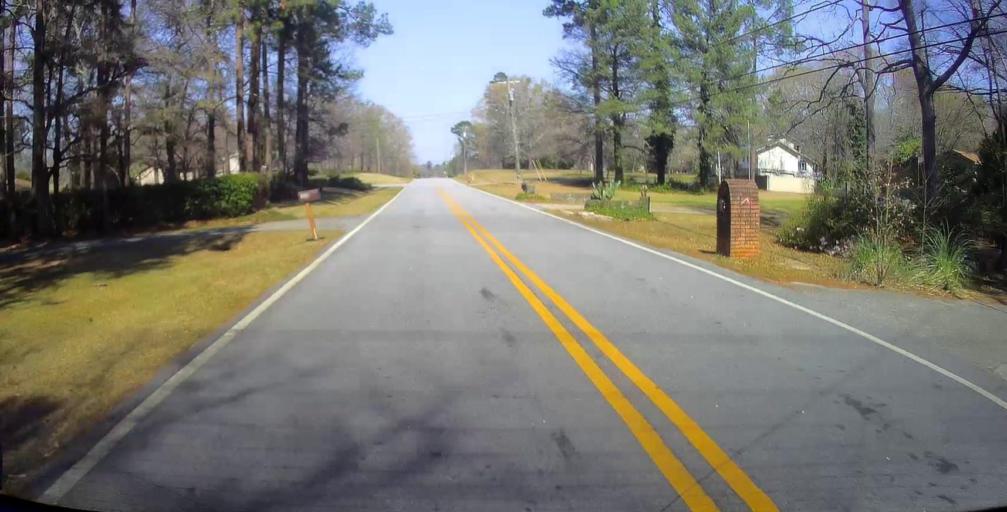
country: US
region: Georgia
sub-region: Houston County
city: Centerville
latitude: 32.5876
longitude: -83.6944
